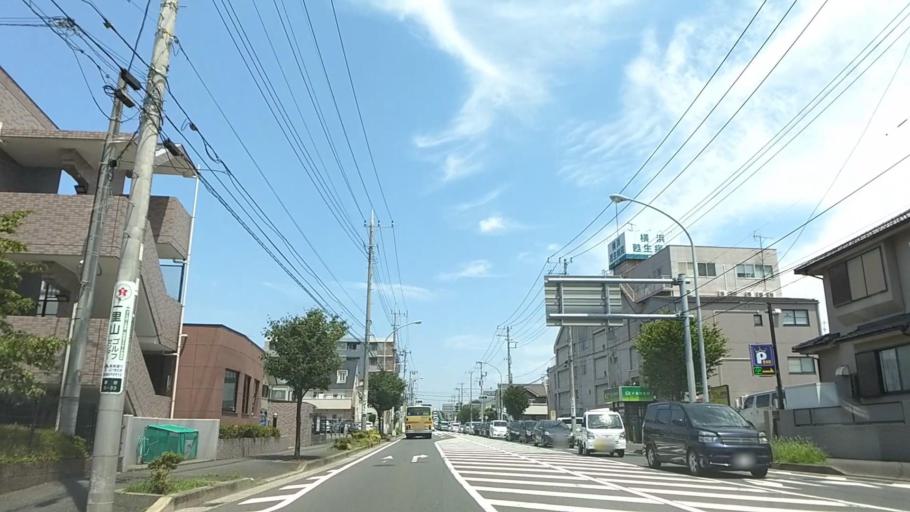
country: JP
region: Kanagawa
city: Minami-rinkan
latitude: 35.4663
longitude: 139.4800
